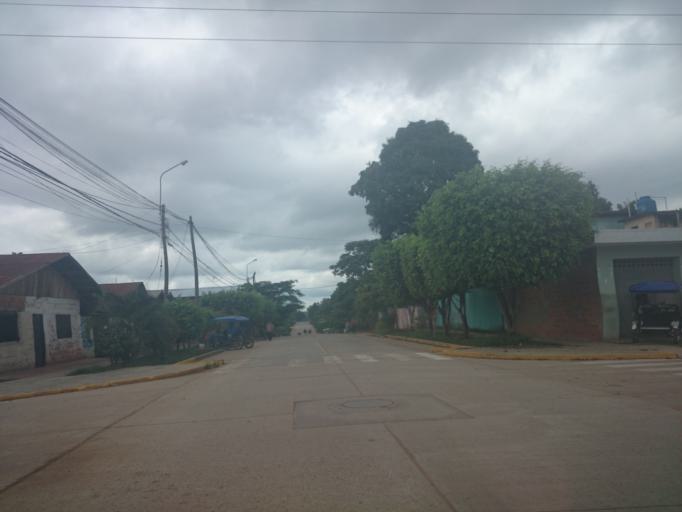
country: PE
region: Ucayali
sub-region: Provincia de Coronel Portillo
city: Puerto Callao
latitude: -8.3616
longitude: -74.5726
